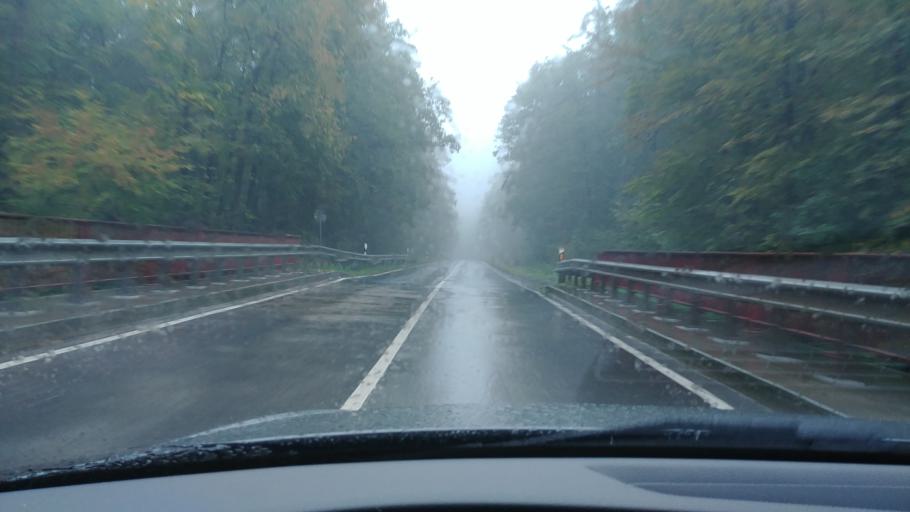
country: DE
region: Rheinland-Pfalz
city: Dohr
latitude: 50.1388
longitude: 7.1337
